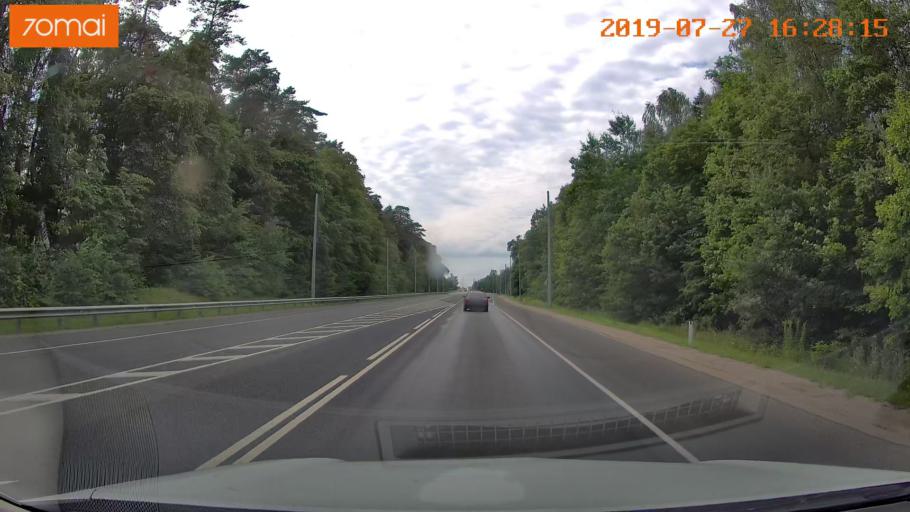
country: RU
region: Kaliningrad
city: Zheleznodorozhnyy
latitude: 54.6473
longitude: 21.3645
